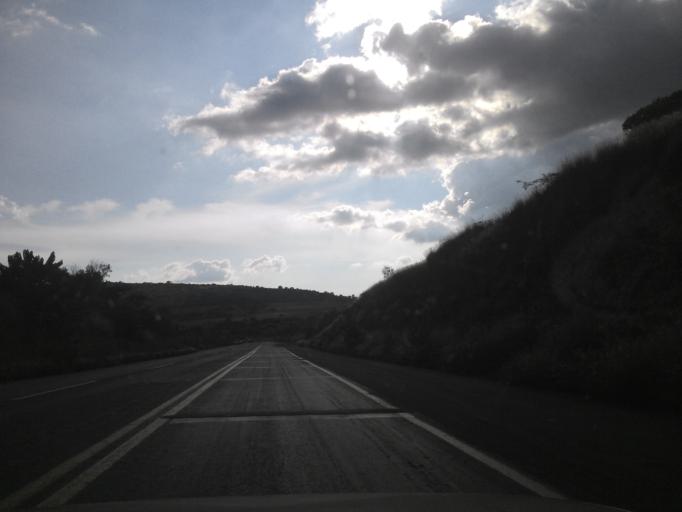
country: MX
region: Jalisco
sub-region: Atotonilco el Alto
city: Ojo de Agua de Moran
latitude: 20.5734
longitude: -102.5316
